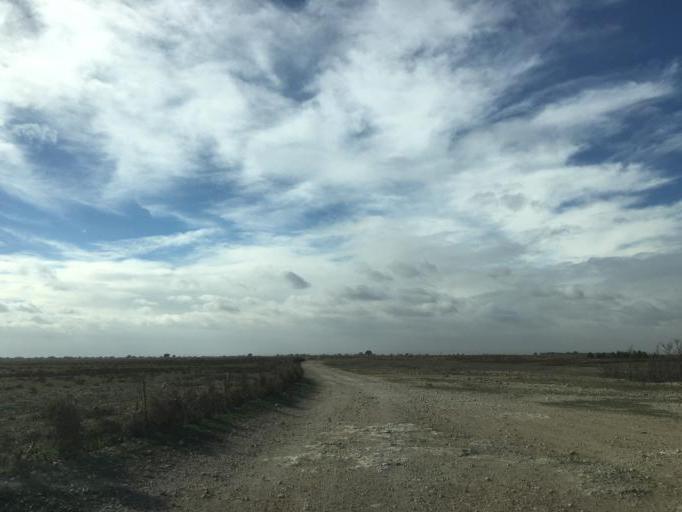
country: ES
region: Castille-La Mancha
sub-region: Provincia de Albacete
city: La Gineta
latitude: 39.0232
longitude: -2.0271
